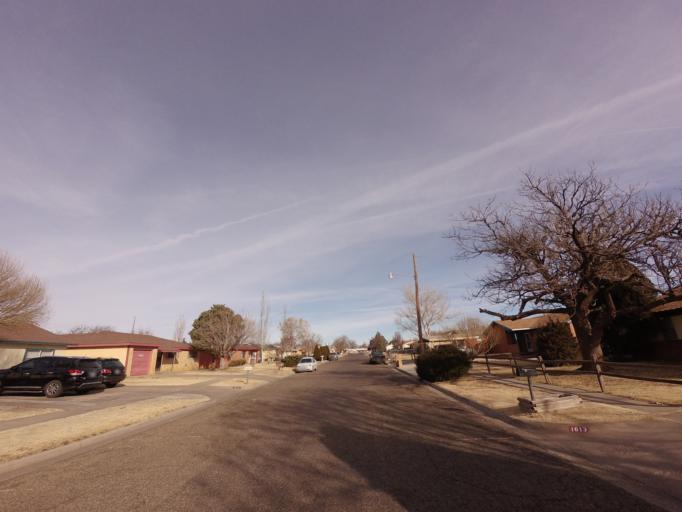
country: US
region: New Mexico
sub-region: Curry County
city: Clovis
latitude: 34.4143
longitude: -103.2210
